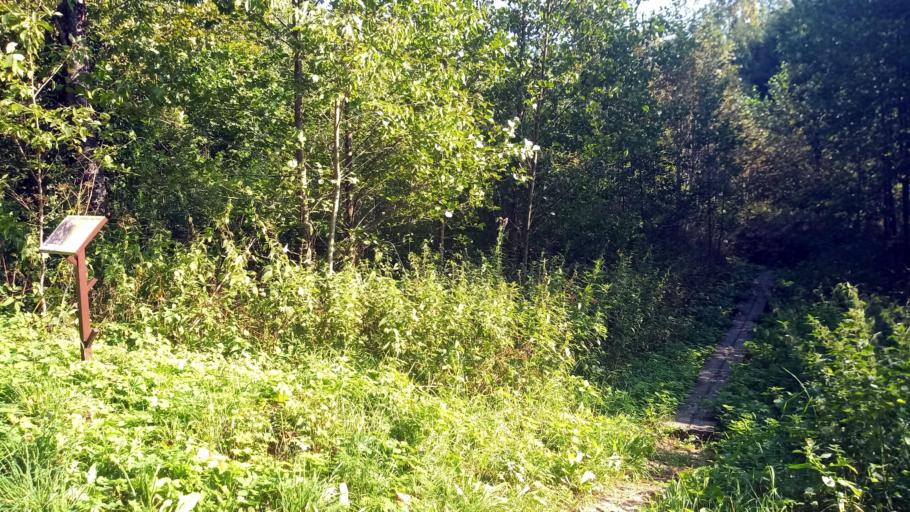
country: LT
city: Varniai
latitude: 55.8802
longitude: 22.3543
